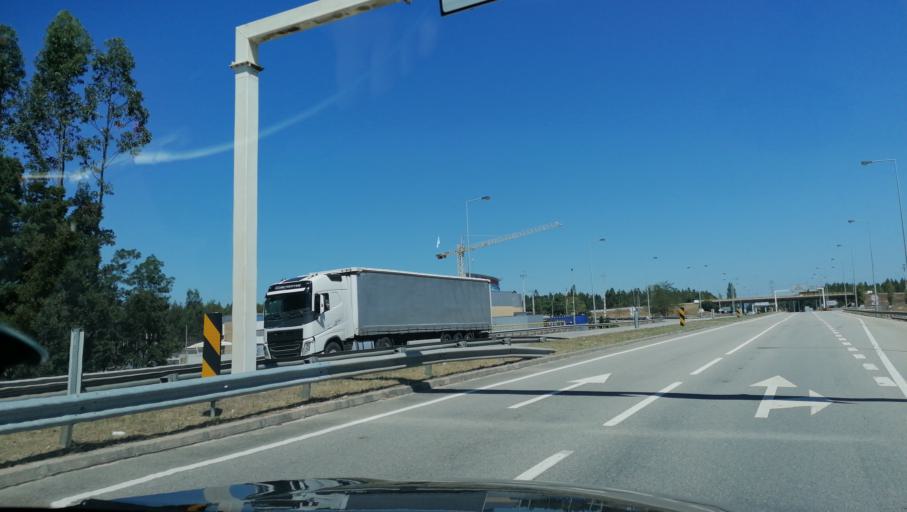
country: PT
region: Aveiro
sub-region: Agueda
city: Agueda
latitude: 40.5921
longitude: -8.4697
